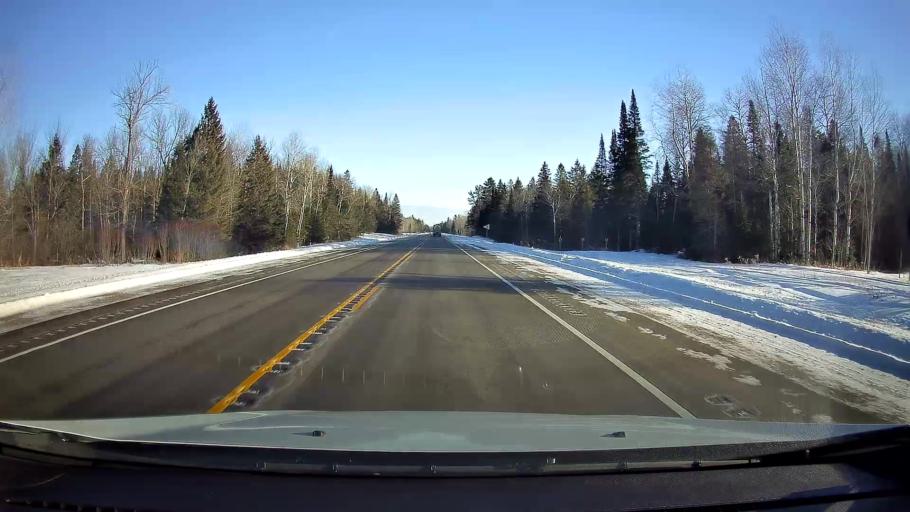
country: US
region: Wisconsin
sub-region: Sawyer County
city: Hayward
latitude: 46.0768
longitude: -91.4078
